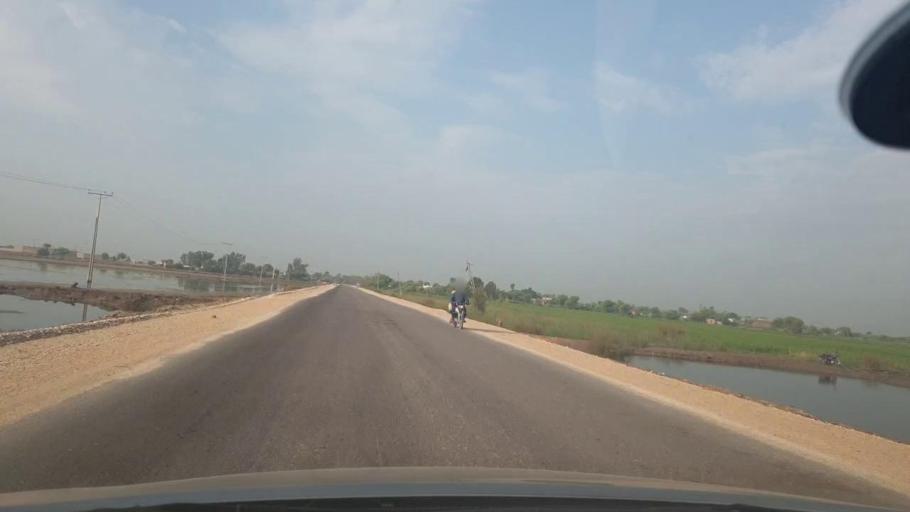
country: PK
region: Sindh
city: Jacobabad
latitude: 28.2196
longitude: 68.3724
